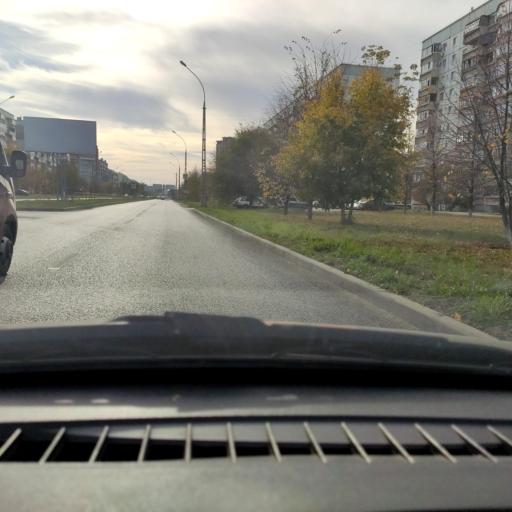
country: RU
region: Samara
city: Tol'yatti
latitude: 53.5457
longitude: 49.3314
